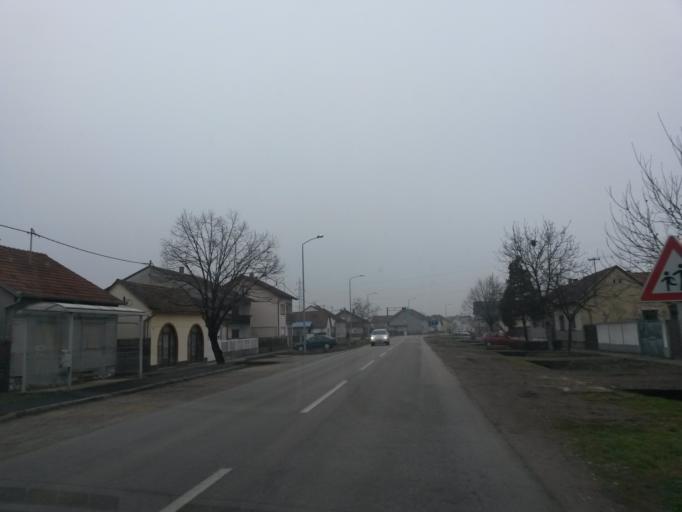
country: HR
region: Vukovarsko-Srijemska
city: Zupanja
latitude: 45.0866
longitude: 18.6990
